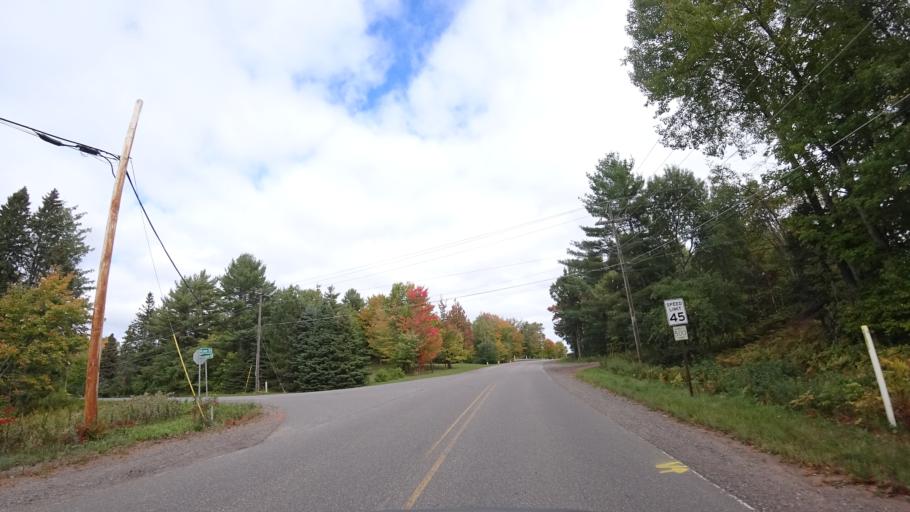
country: US
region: Michigan
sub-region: Marquette County
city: Trowbridge Park
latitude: 46.5354
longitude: -87.4377
